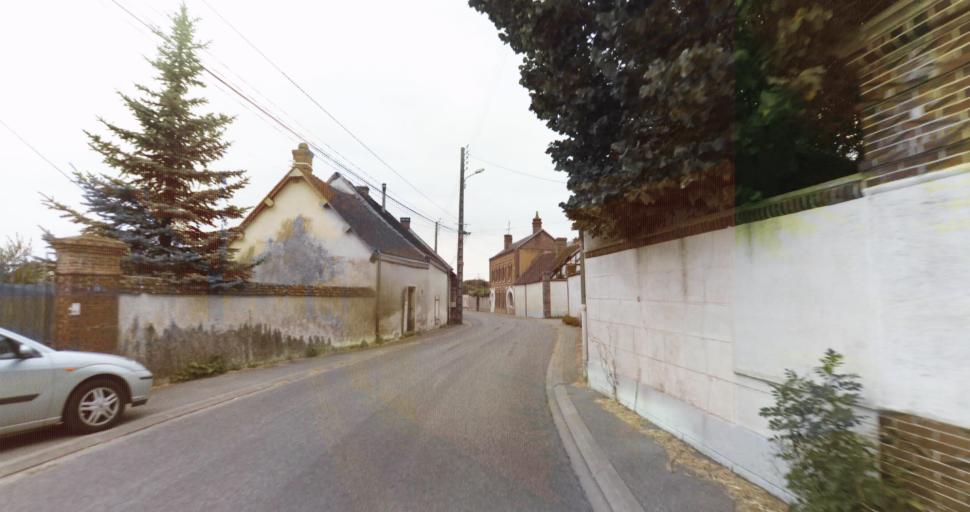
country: FR
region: Haute-Normandie
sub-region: Departement de l'Eure
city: Saint-Germain-sur-Avre
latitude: 48.8163
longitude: 1.2843
